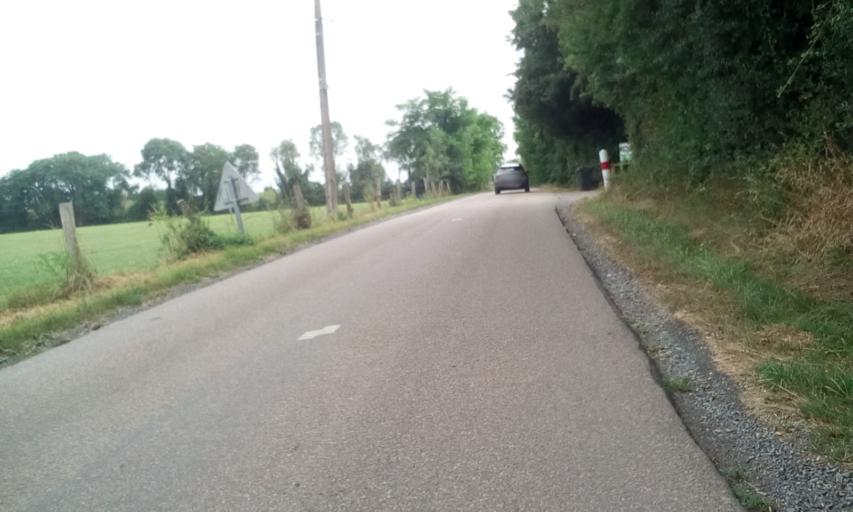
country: FR
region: Lower Normandy
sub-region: Departement du Calvados
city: Bavent
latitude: 49.2115
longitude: -0.1788
